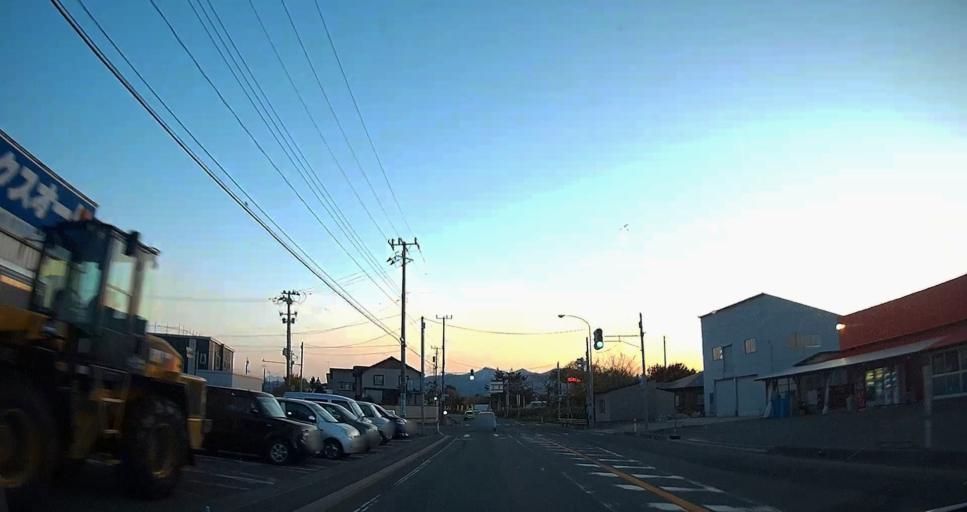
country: JP
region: Aomori
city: Misawa
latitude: 40.8758
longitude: 141.1405
